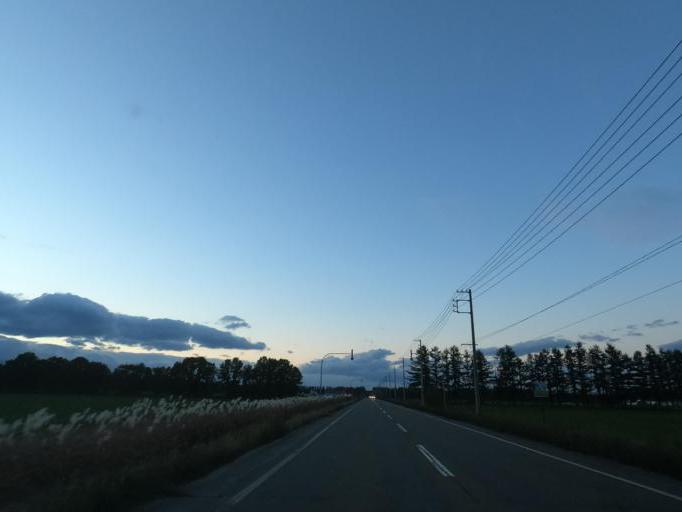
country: JP
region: Hokkaido
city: Obihiro
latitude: 42.6662
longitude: 143.1757
